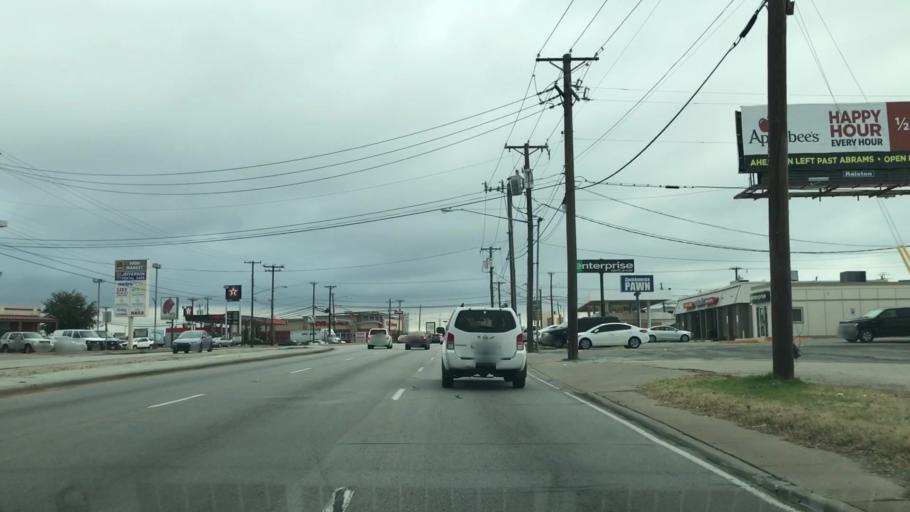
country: US
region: Texas
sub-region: Dallas County
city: Highland Park
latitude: 32.8564
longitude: -96.7477
